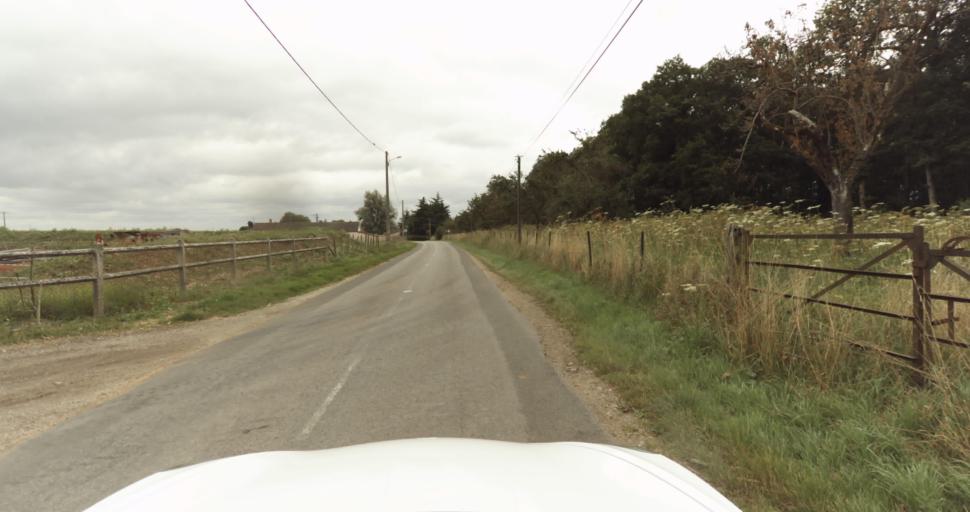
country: FR
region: Haute-Normandie
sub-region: Departement de l'Eure
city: Arnieres-sur-Iton
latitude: 48.9366
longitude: 1.0792
